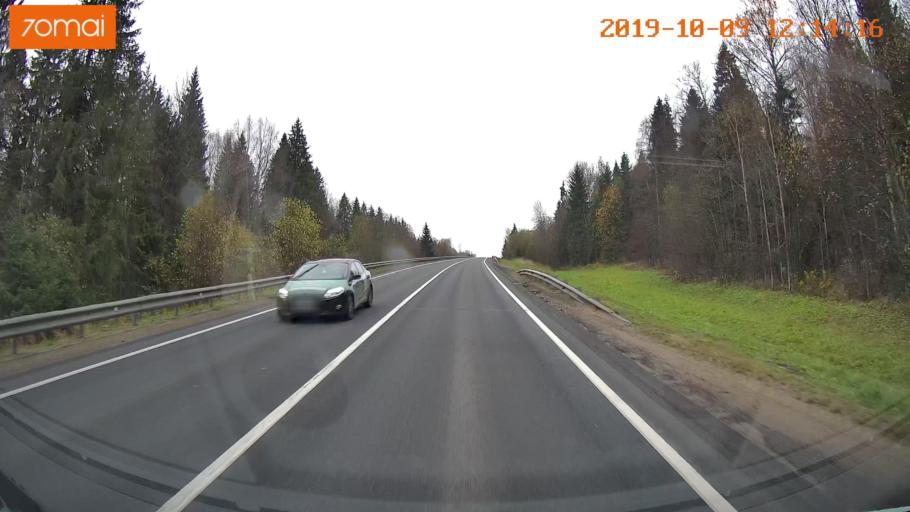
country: RU
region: Jaroslavl
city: Prechistoye
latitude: 58.4984
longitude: 40.3389
